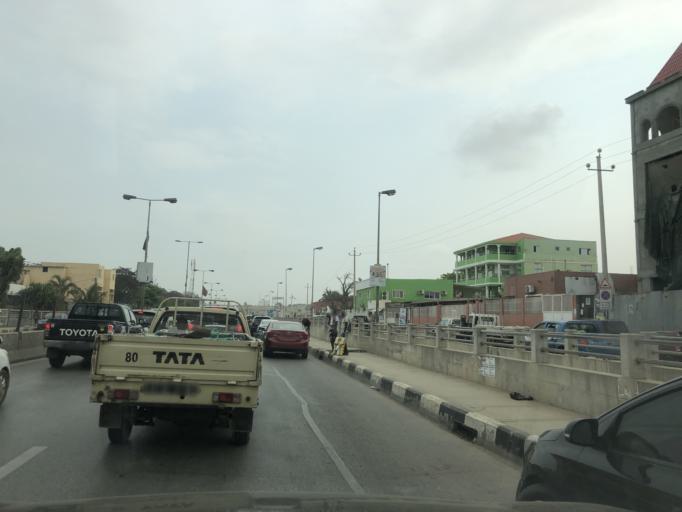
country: AO
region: Luanda
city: Luanda
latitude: -8.8519
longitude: 13.2094
